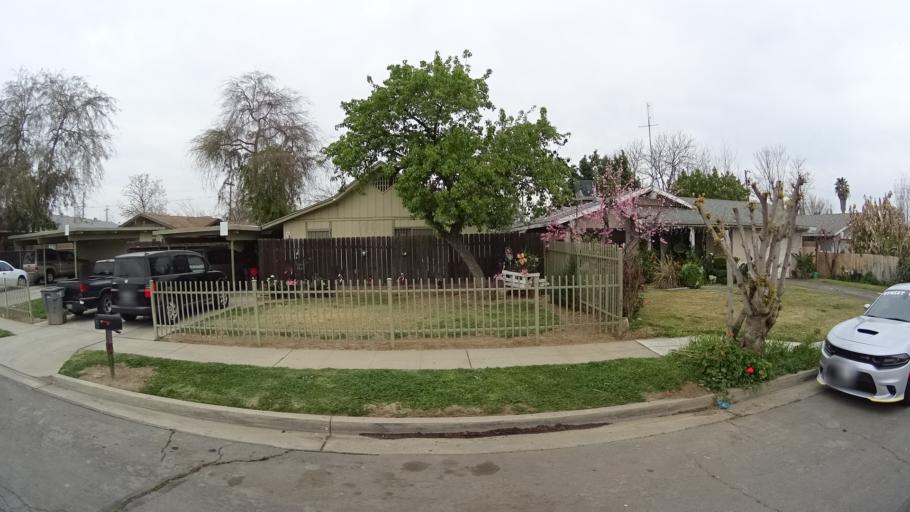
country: US
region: California
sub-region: Fresno County
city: Clovis
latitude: 36.8409
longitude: -119.7964
